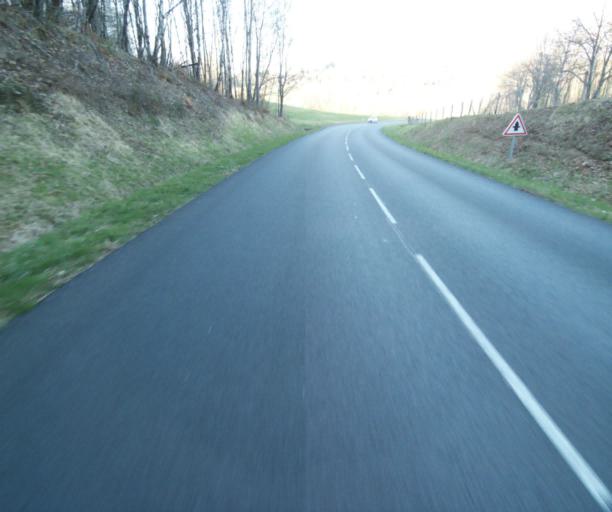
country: FR
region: Limousin
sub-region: Departement de la Correze
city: Seilhac
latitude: 45.3566
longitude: 1.7088
